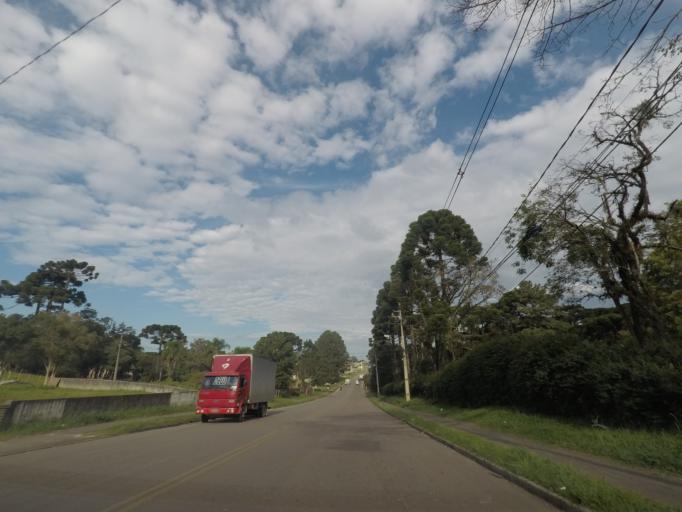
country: BR
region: Parana
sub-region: Sao Jose Dos Pinhais
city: Sao Jose dos Pinhais
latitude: -25.5701
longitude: -49.2817
